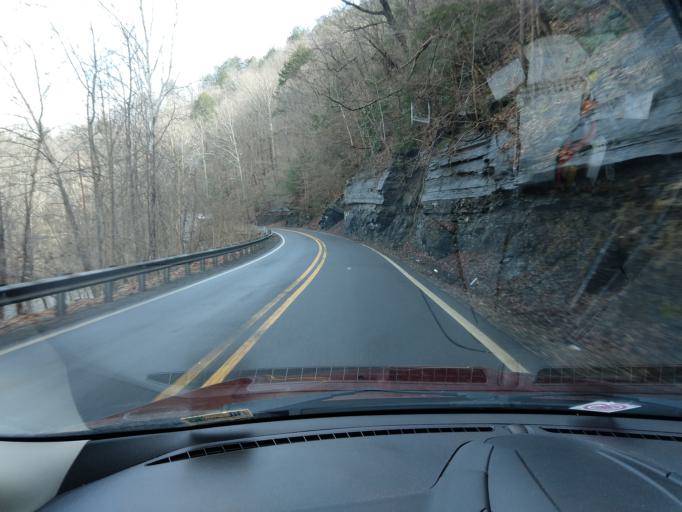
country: US
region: West Virginia
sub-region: McDowell County
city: Welch
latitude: 37.3416
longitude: -81.7255
